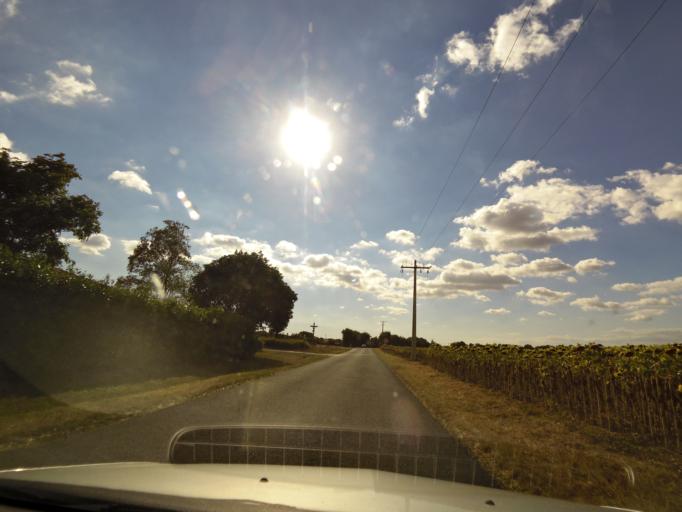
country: FR
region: Poitou-Charentes
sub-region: Departement des Deux-Sevres
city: Beauvoir-sur-Niort
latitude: 46.1490
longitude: -0.4605
